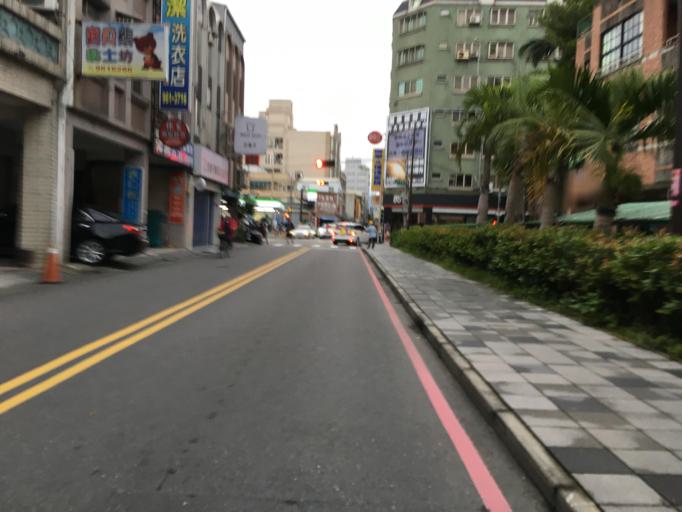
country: TW
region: Taiwan
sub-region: Yilan
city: Yilan
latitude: 24.6778
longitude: 121.7605
